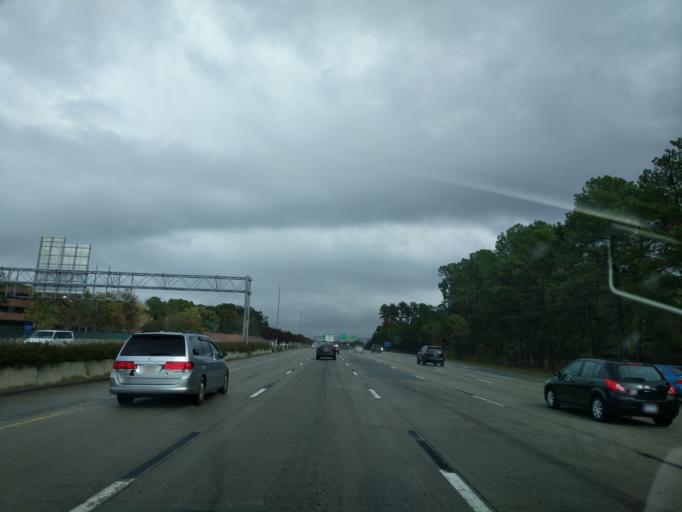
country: US
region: North Carolina
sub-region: Durham County
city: Durham
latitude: 36.0260
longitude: -78.9426
